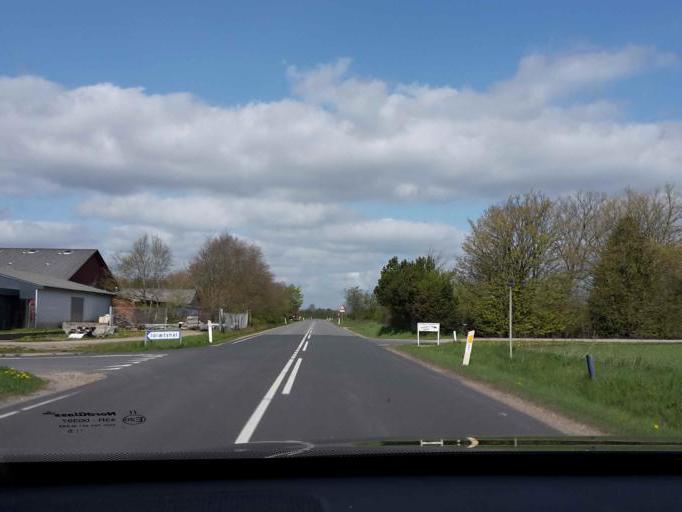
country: DK
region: South Denmark
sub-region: Varde Kommune
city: Olgod
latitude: 55.7118
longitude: 8.7463
